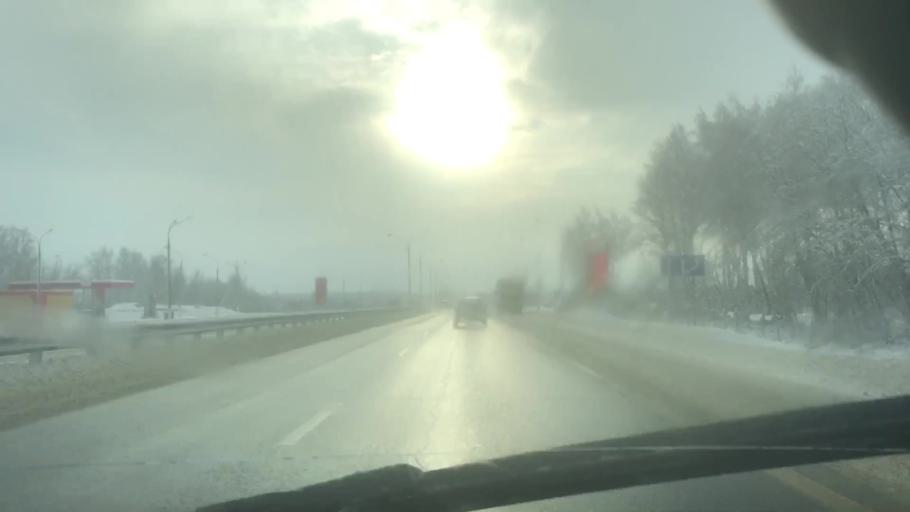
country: RU
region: Tula
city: Venev
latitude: 54.2822
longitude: 38.1594
